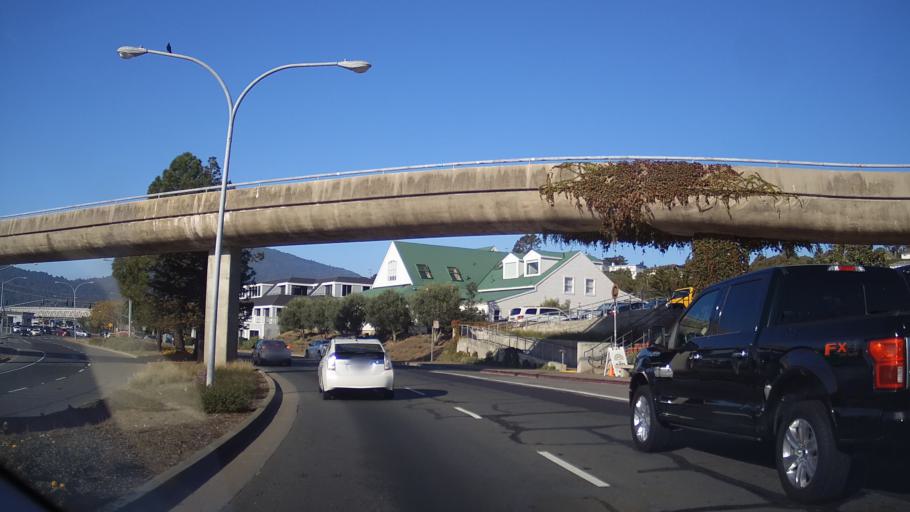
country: US
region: California
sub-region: Marin County
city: Corte Madera
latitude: 37.9466
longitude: -122.5100
